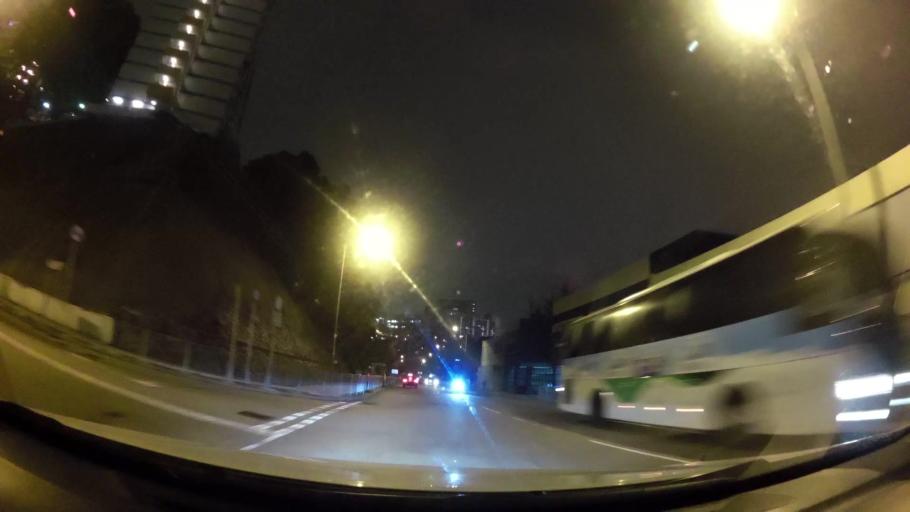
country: HK
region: Sham Shui Po
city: Sham Shui Po
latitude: 22.3444
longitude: 114.1294
